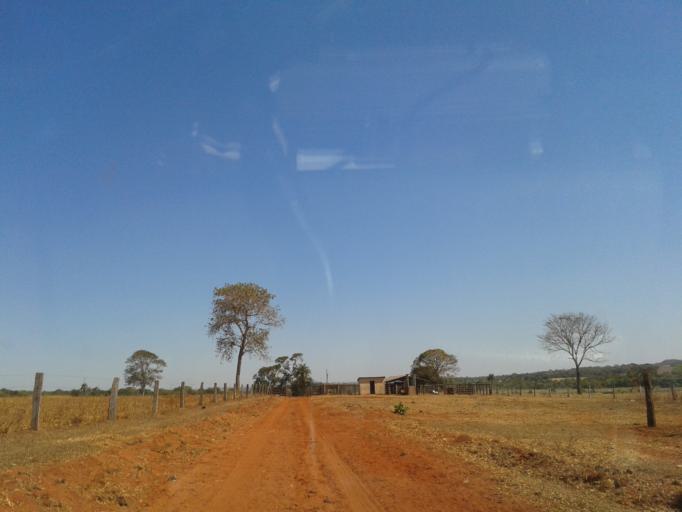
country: BR
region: Minas Gerais
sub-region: Santa Vitoria
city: Santa Vitoria
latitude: -19.0839
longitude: -50.0733
